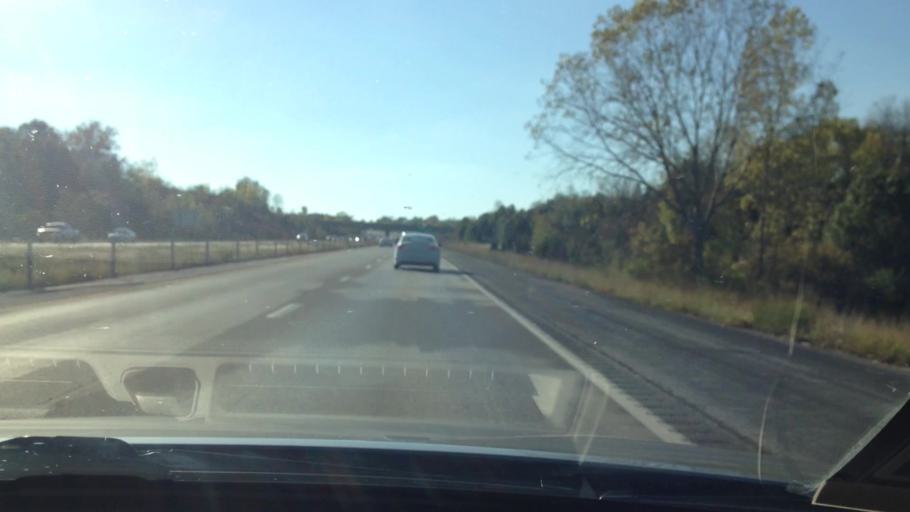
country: US
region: Missouri
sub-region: Clay County
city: Gladstone
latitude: 39.2605
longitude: -94.5821
